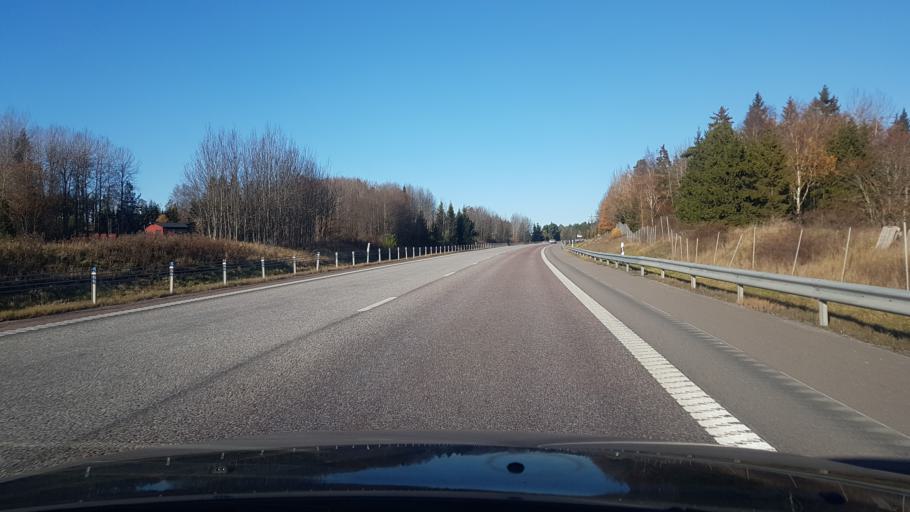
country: SE
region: Uppsala
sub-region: Uppsala Kommun
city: Alsike
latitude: 59.7797
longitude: 17.7805
